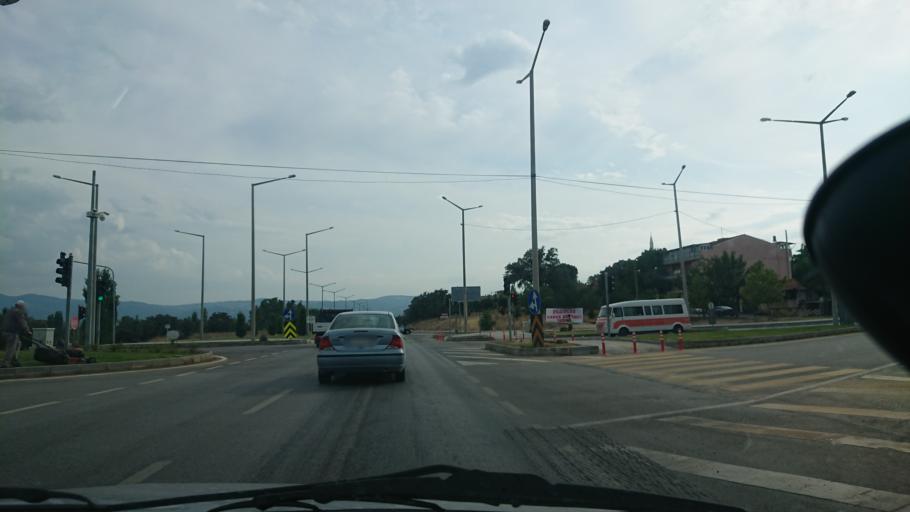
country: TR
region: Kuetahya
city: Gediz
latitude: 39.0001
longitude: 29.4034
